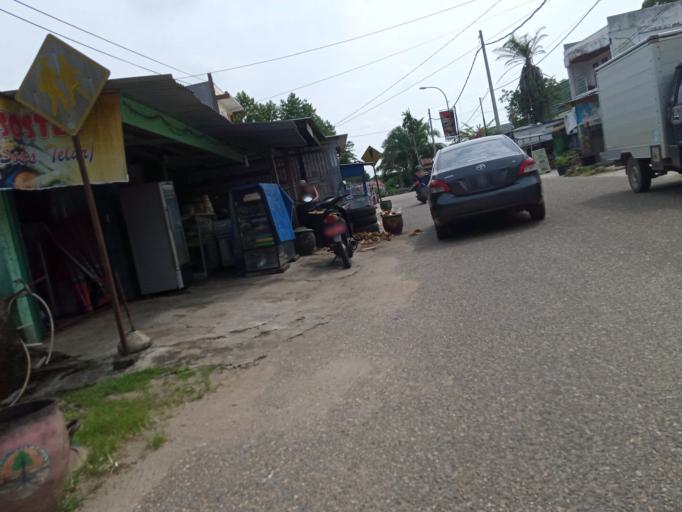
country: ID
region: Jambi
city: Muara Bulian
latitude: -1.7113
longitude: 103.2596
